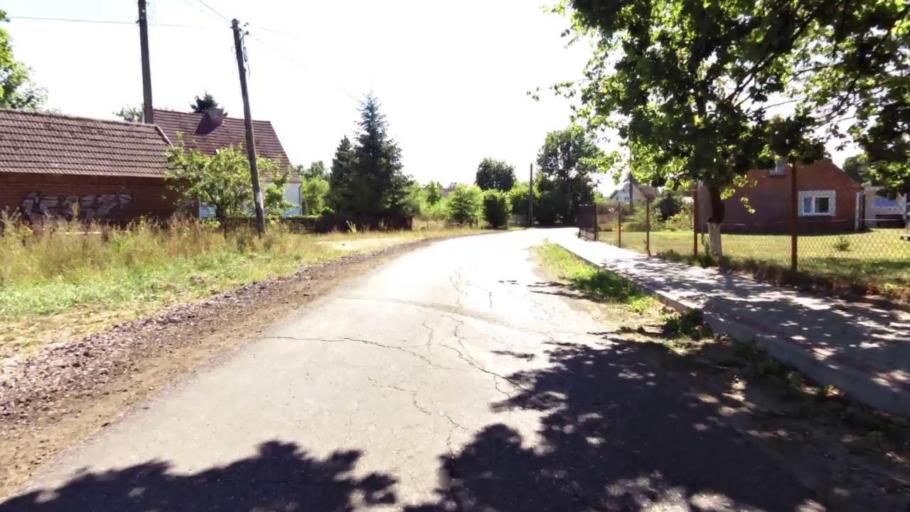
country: PL
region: West Pomeranian Voivodeship
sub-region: Powiat szczecinecki
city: Szczecinek
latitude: 53.6876
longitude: 16.6037
